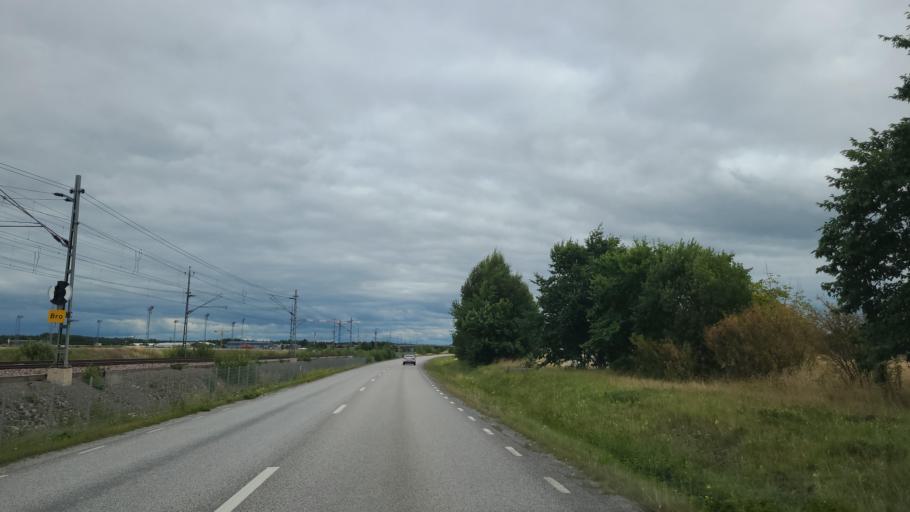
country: SE
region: Stockholm
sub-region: Upplands-Bro Kommun
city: Bro
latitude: 59.5209
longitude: 17.6030
